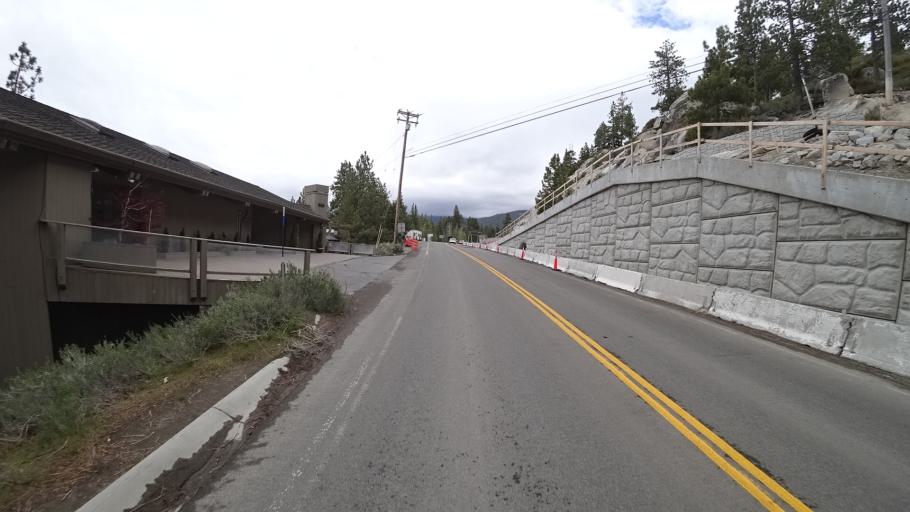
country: US
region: Nevada
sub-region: Washoe County
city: Incline Village
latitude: 39.2303
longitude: -119.9320
